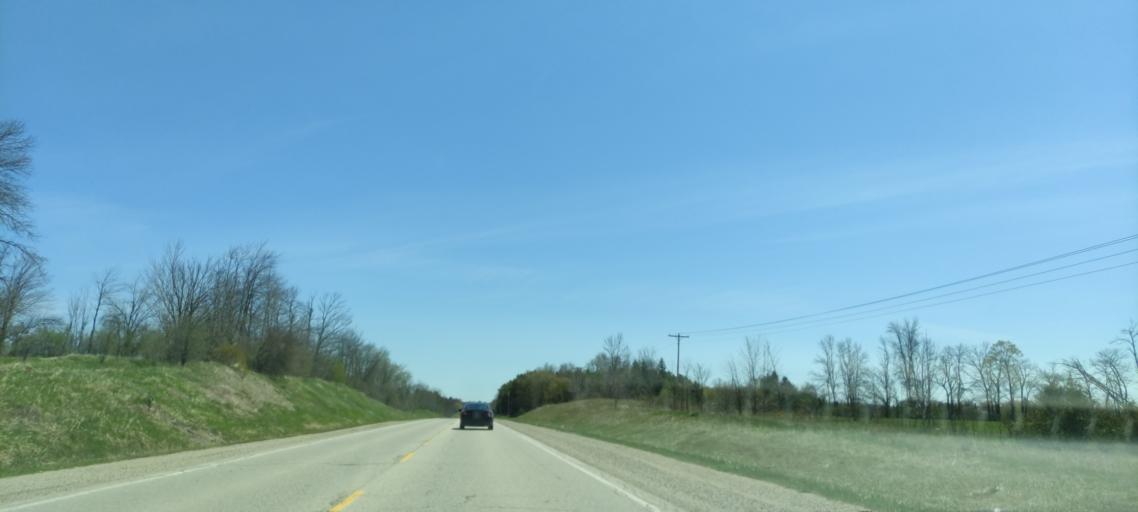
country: CA
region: Ontario
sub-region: Wellington County
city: Guelph
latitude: 43.5745
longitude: -80.3908
